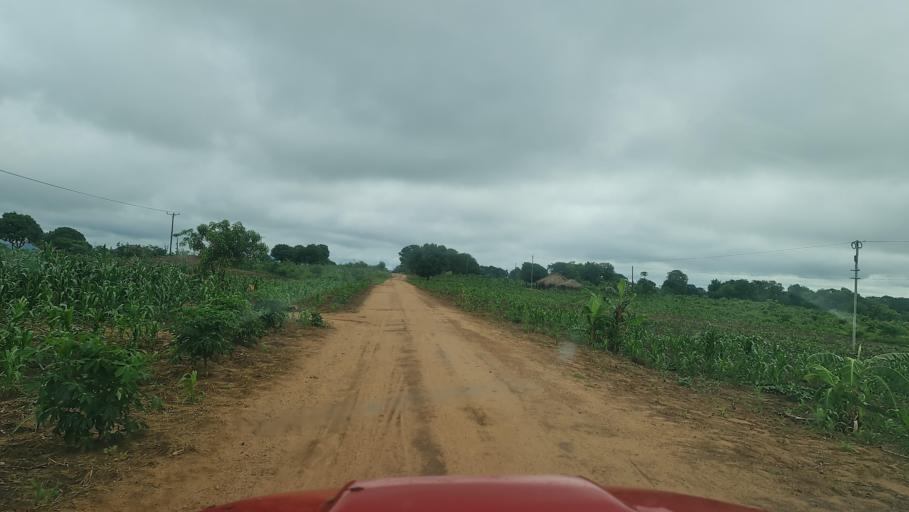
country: MW
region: Southern Region
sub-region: Nsanje District
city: Nsanje
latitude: -17.1973
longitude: 35.8430
